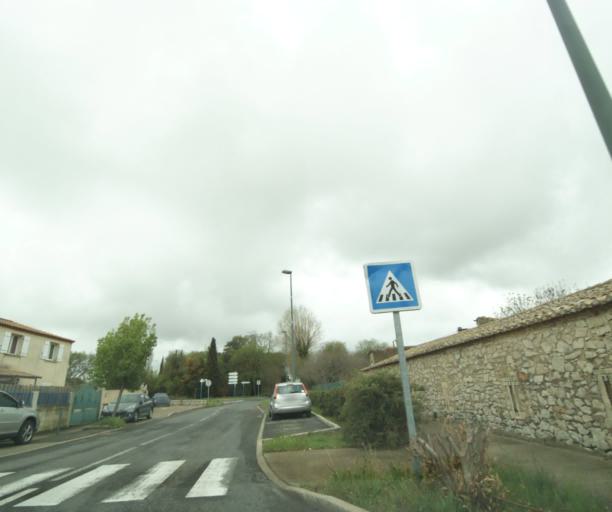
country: FR
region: Languedoc-Roussillon
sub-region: Departement de l'Herault
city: Cournonterral
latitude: 43.5599
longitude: 3.7257
